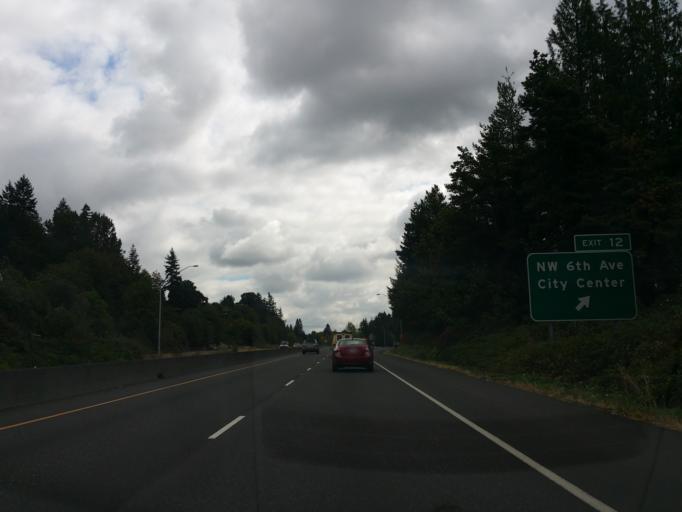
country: US
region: Washington
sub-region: Clark County
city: Camas
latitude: 45.5800
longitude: -122.4366
